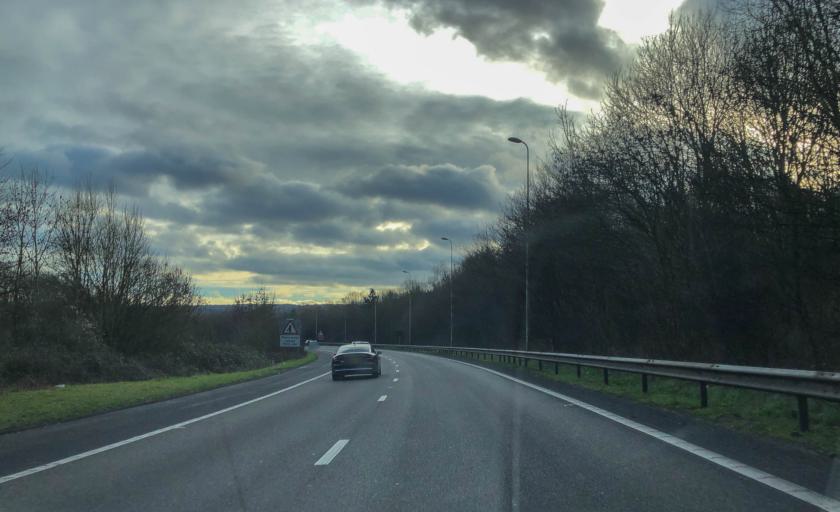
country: GB
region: England
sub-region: Kent
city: Halstead
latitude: 51.2992
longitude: 0.1468
